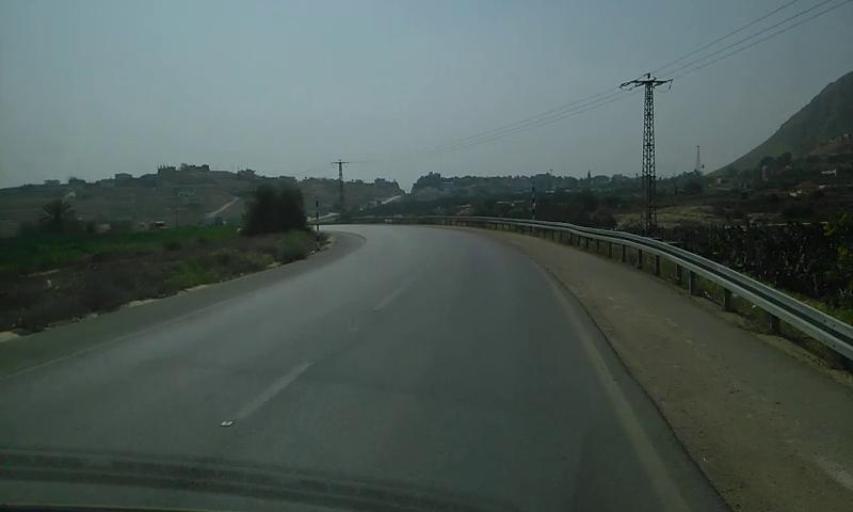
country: PS
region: West Bank
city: An Nuway`imah
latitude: 31.8841
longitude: 35.4362
